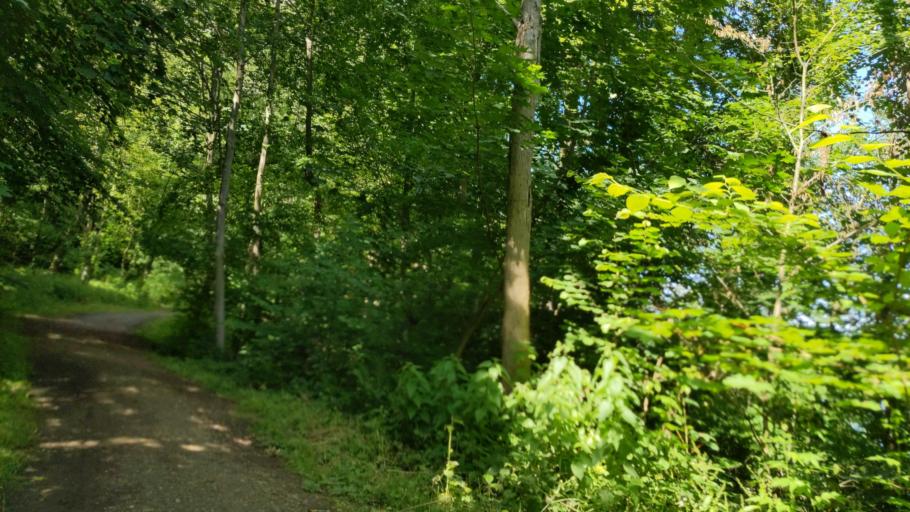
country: DE
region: Schleswig-Holstein
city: Romnitz
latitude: 53.6918
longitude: 10.7566
